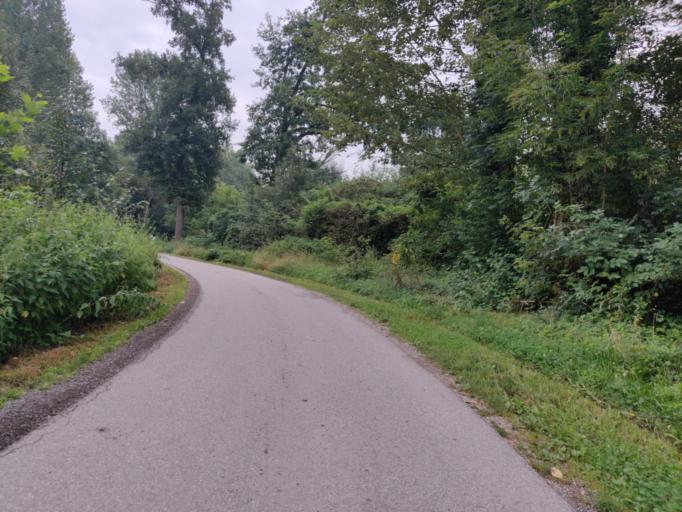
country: AT
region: Upper Austria
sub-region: Politischer Bezirk Linz-Land
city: Asten
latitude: 48.2353
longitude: 14.4247
